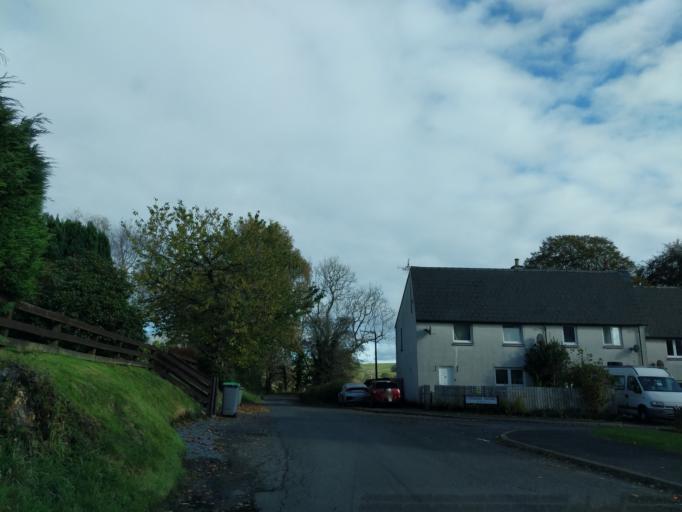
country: GB
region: Scotland
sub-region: Dumfries and Galloway
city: Castle Douglas
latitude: 55.0743
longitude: -4.1388
